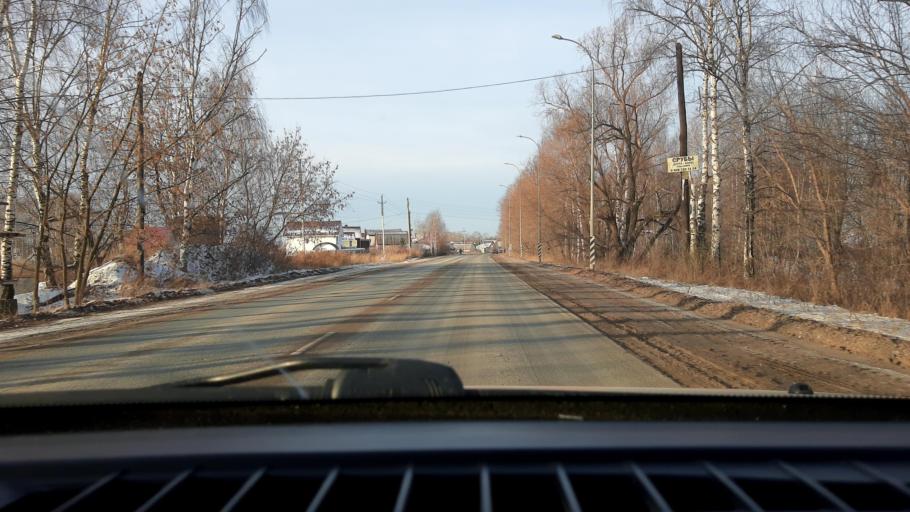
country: RU
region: Nizjnij Novgorod
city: Bor
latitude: 56.3787
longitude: 44.0480
